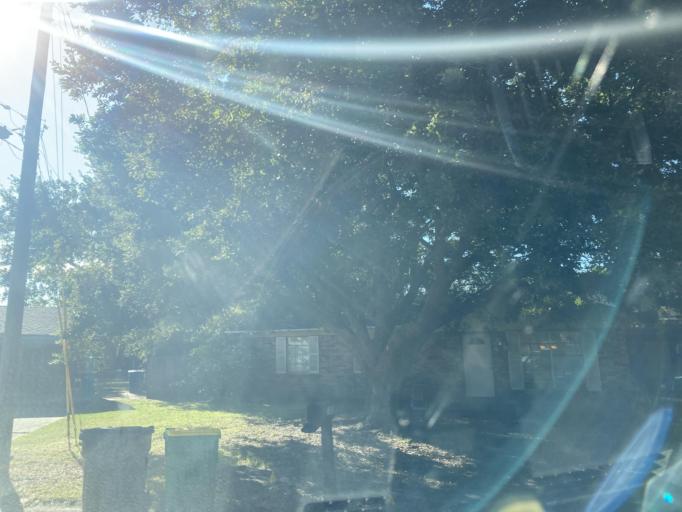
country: US
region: Mississippi
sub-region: Jackson County
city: Saint Martin
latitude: 30.4460
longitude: -88.8807
